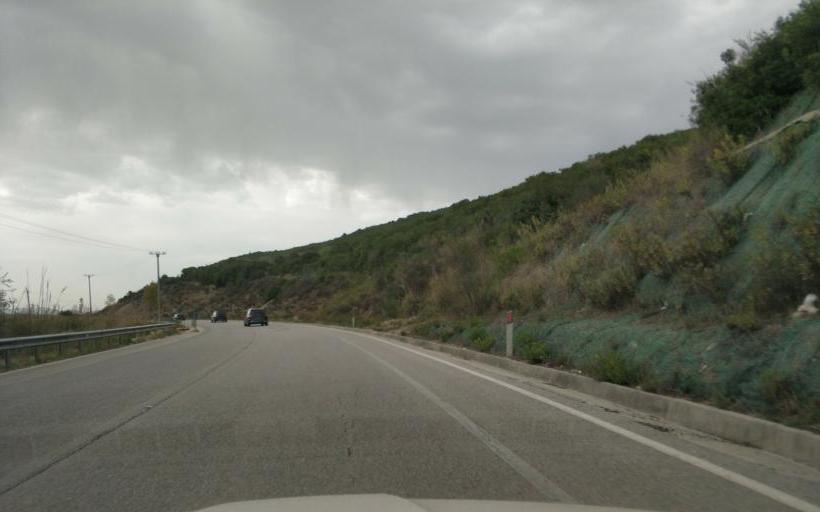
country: AL
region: Fier
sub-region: Rrethi i Mallakastres
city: Hekal
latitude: 40.5273
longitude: 19.7327
